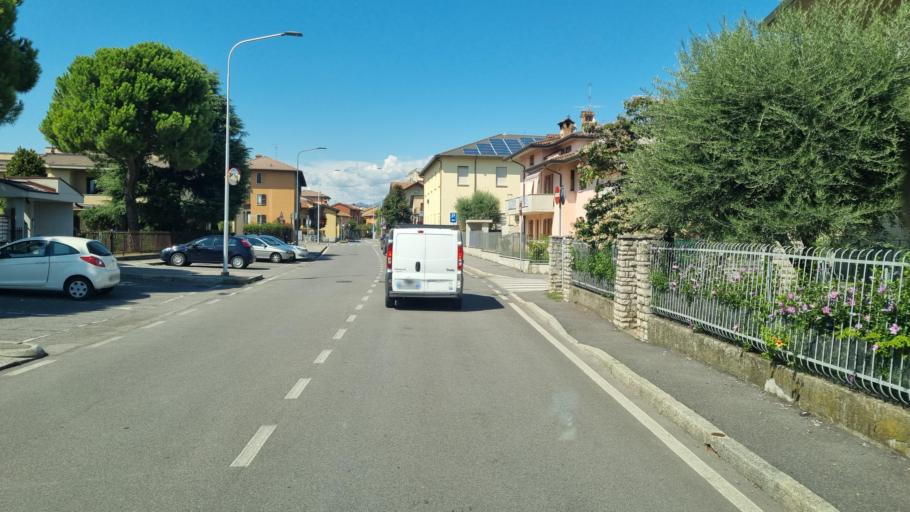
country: IT
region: Lombardy
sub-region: Provincia di Bergamo
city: Azzano San Paolo
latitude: 45.6589
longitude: 9.6753
